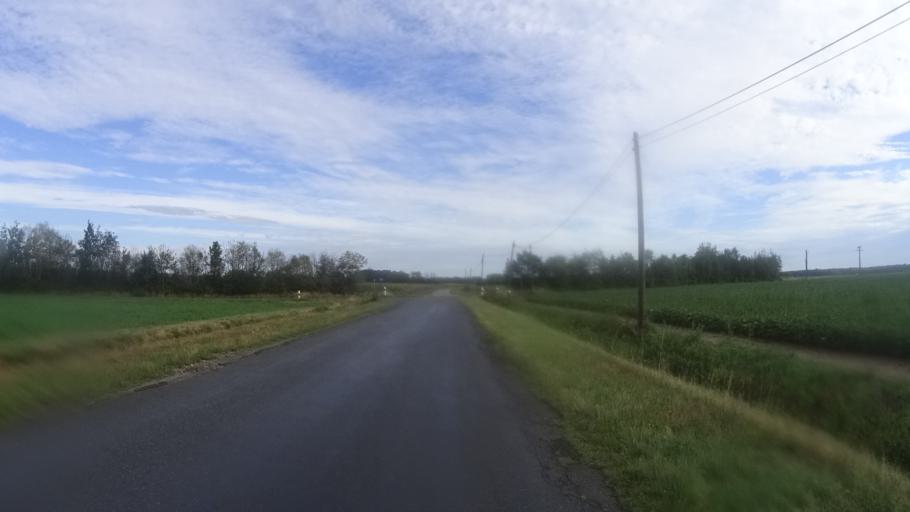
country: FR
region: Centre
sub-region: Departement du Loiret
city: Chateauneuf-sur-Loire
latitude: 47.8861
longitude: 2.2128
